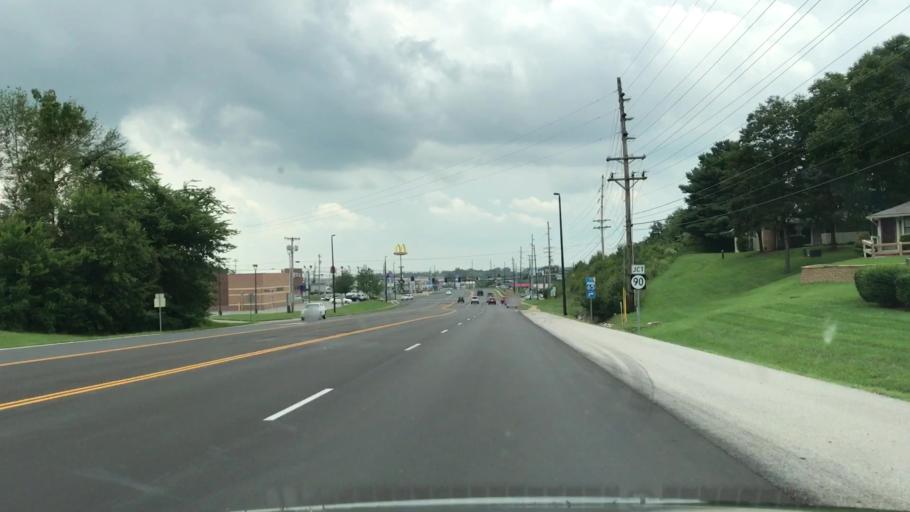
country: US
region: Kentucky
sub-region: Barren County
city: Glasgow
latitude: 37.0114
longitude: -85.9196
